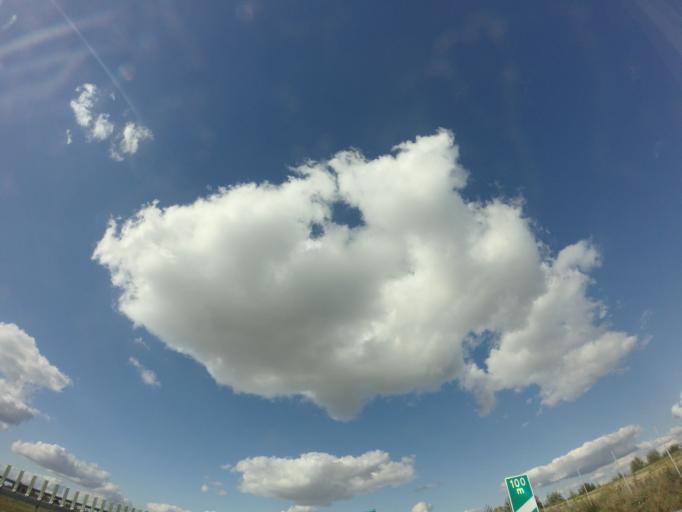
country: PL
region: Lower Silesian Voivodeship
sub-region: Powiat trzebnicki
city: Trzebnica
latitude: 51.2965
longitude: 17.0369
